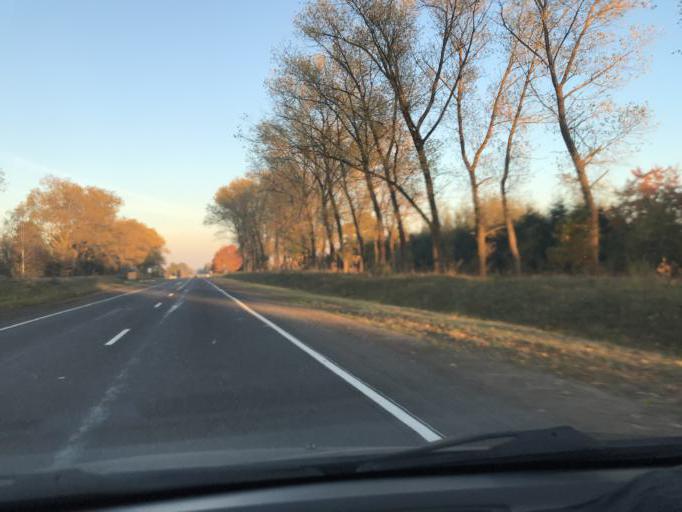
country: BY
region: Minsk
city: Staryya Darohi
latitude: 53.0591
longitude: 28.4691
